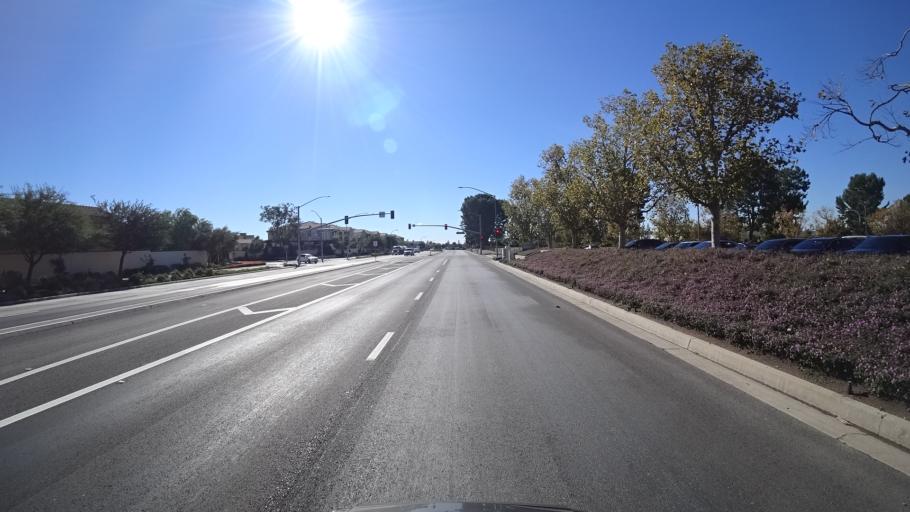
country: US
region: California
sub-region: Orange County
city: Yorba Linda
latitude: 33.9132
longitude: -117.8503
